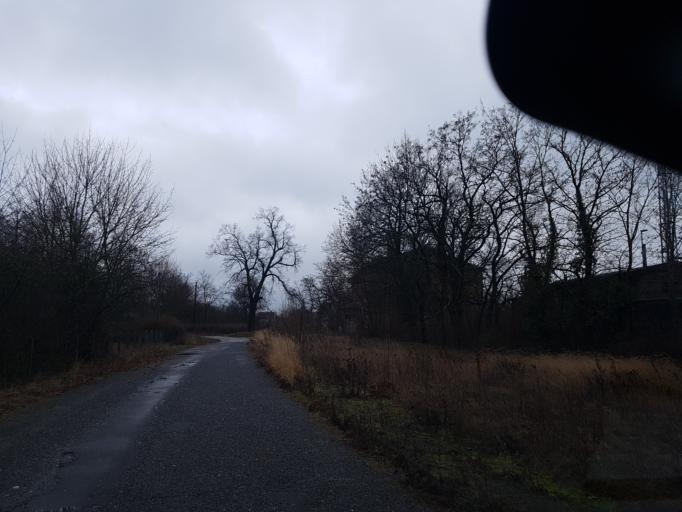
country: DE
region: Brandenburg
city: Muhlberg
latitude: 51.4672
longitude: 13.2943
